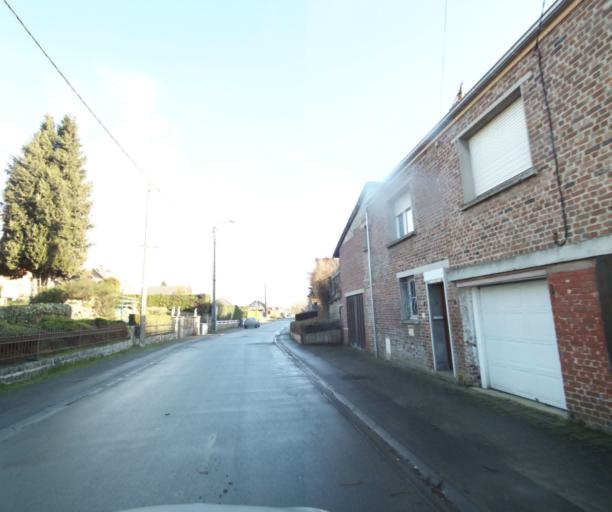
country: FR
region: Nord-Pas-de-Calais
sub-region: Departement du Nord
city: Saultain
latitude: 50.3360
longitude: 3.5844
